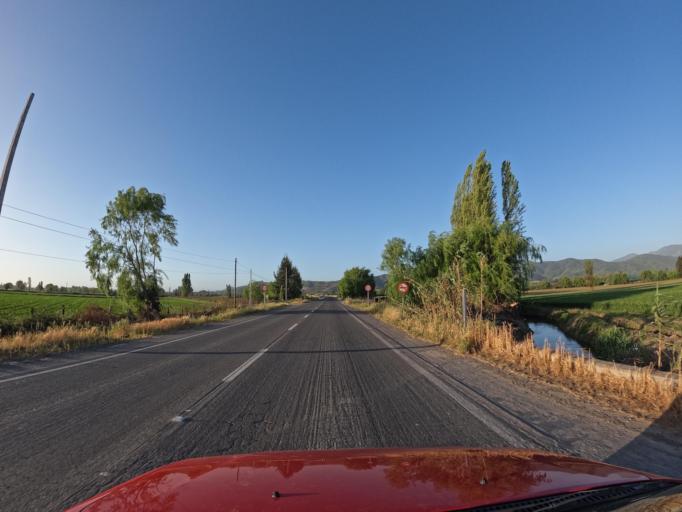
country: CL
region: O'Higgins
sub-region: Provincia de Cachapoal
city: San Vicente
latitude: -34.2886
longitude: -71.3677
